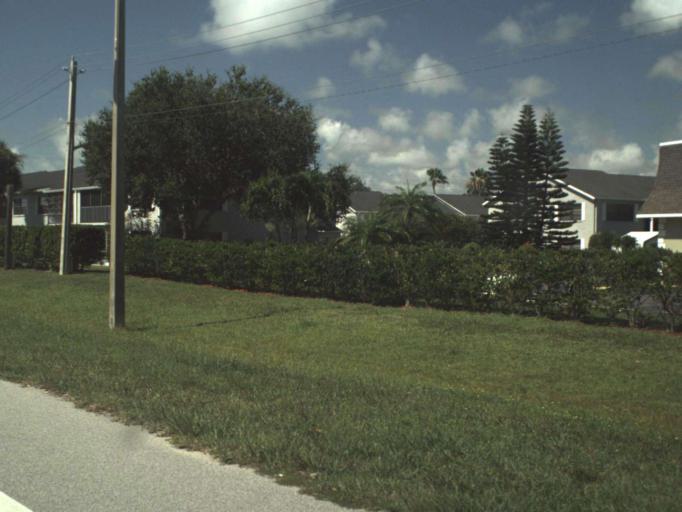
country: US
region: Florida
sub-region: Indian River County
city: Vero Beach
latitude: 27.6361
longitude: -80.3799
